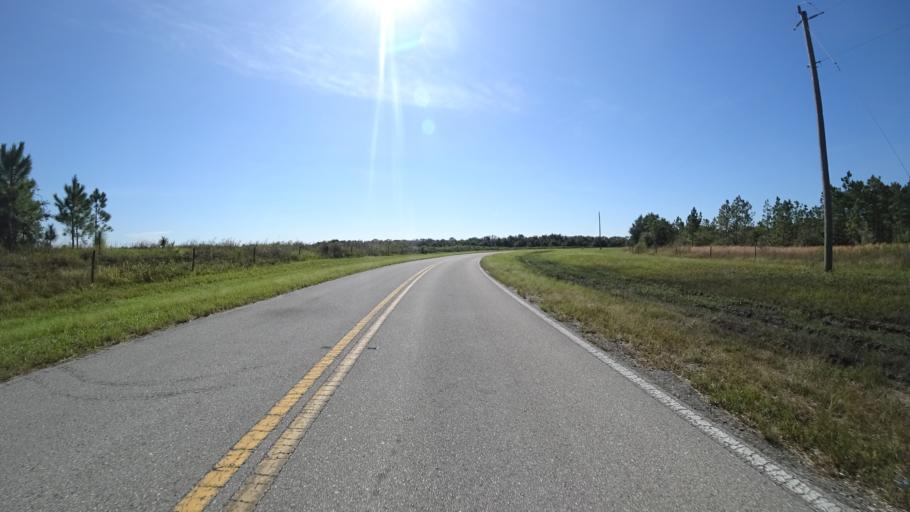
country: US
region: Florida
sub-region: Hillsborough County
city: Wimauma
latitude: 27.5897
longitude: -82.1809
